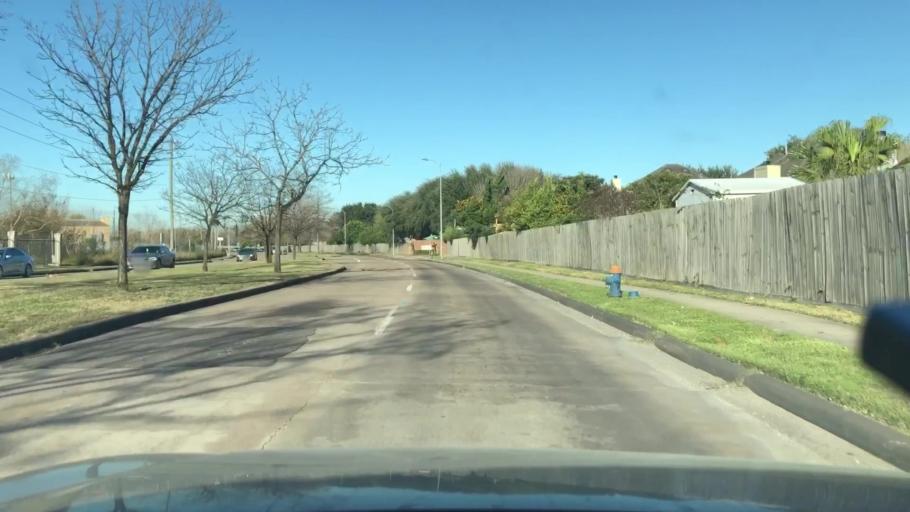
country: US
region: Texas
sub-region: Fort Bend County
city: Missouri City
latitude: 29.6449
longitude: -95.5322
